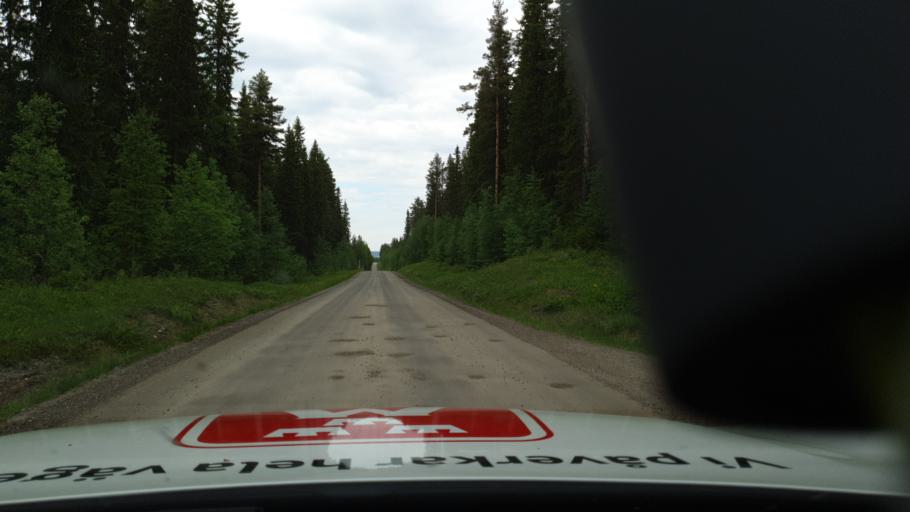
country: SE
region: Jaemtland
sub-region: Braecke Kommun
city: Braecke
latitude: 63.1168
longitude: 15.7491
